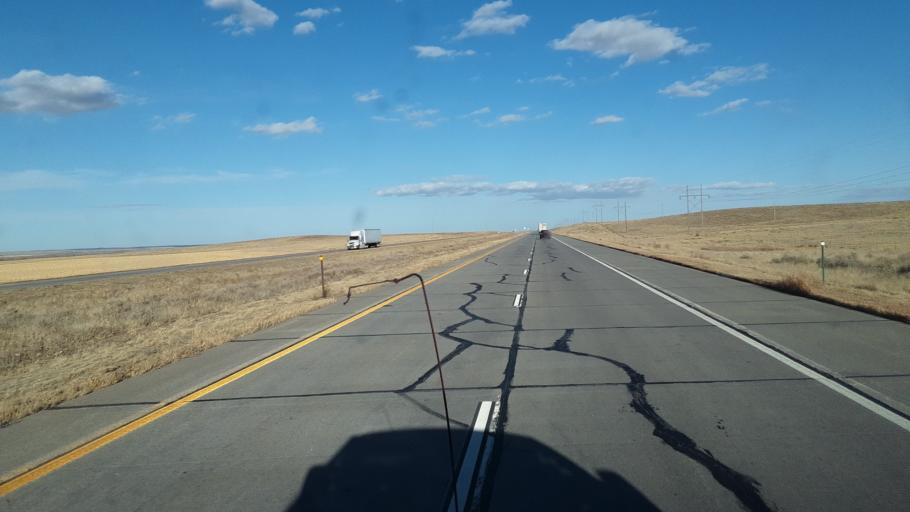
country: US
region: Nebraska
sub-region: Cheyenne County
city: Sidney
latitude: 40.7945
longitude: -102.8819
